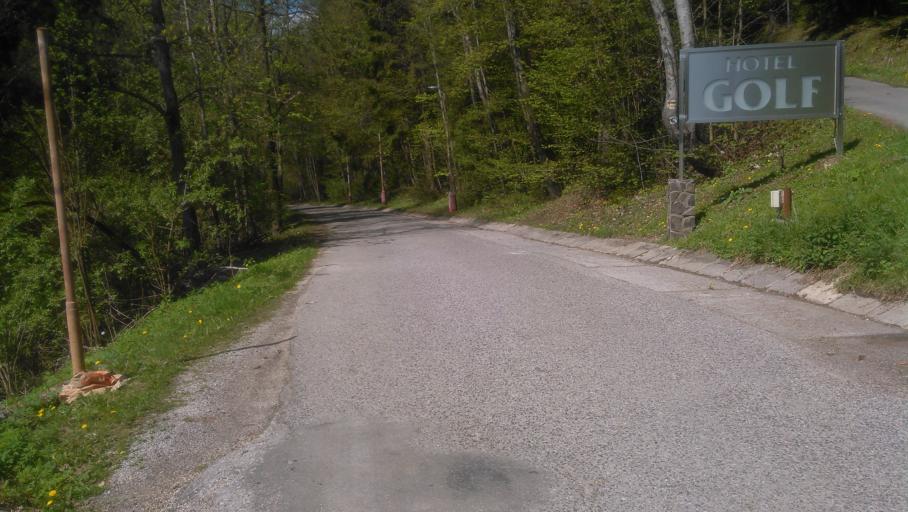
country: SK
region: Banskobystricky
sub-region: Okres Banska Bystrica
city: Brezno
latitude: 48.8750
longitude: 19.5966
